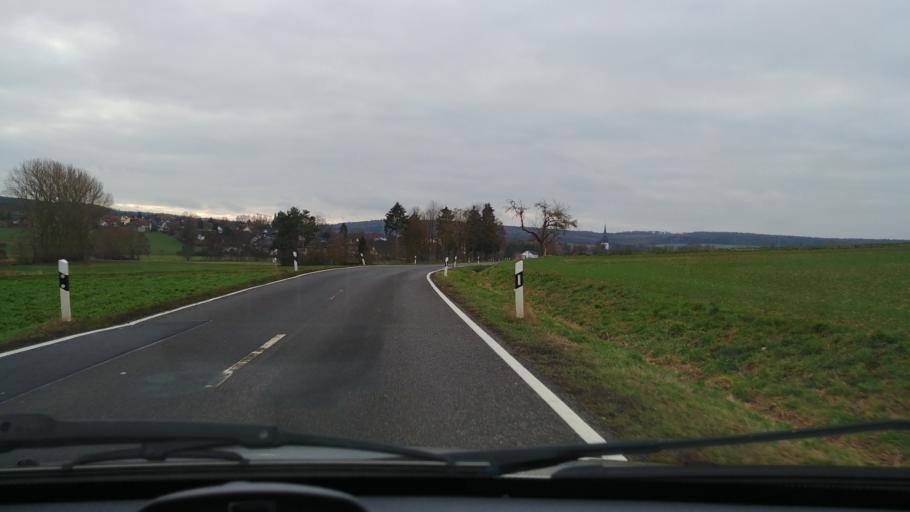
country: DE
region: Rheinland-Pfalz
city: Netzbach
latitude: 50.3181
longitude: 8.1639
